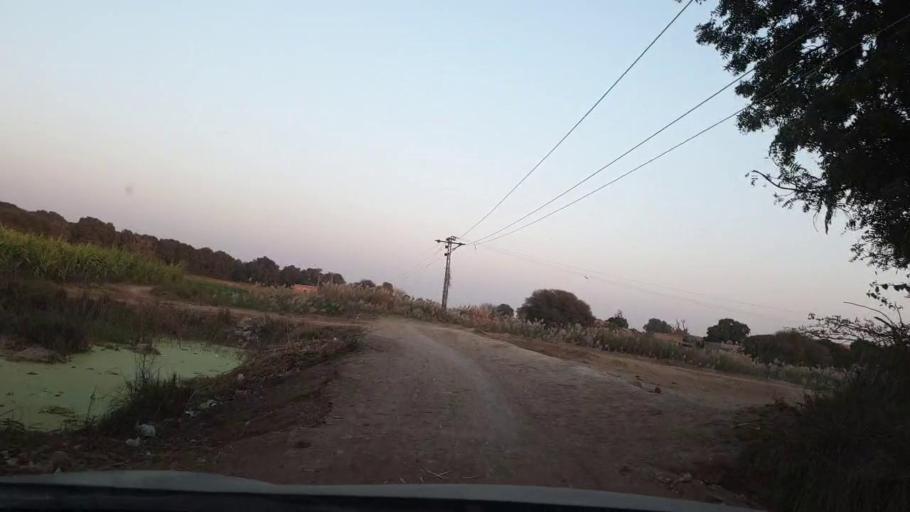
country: PK
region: Sindh
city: Tando Allahyar
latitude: 25.5058
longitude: 68.7495
